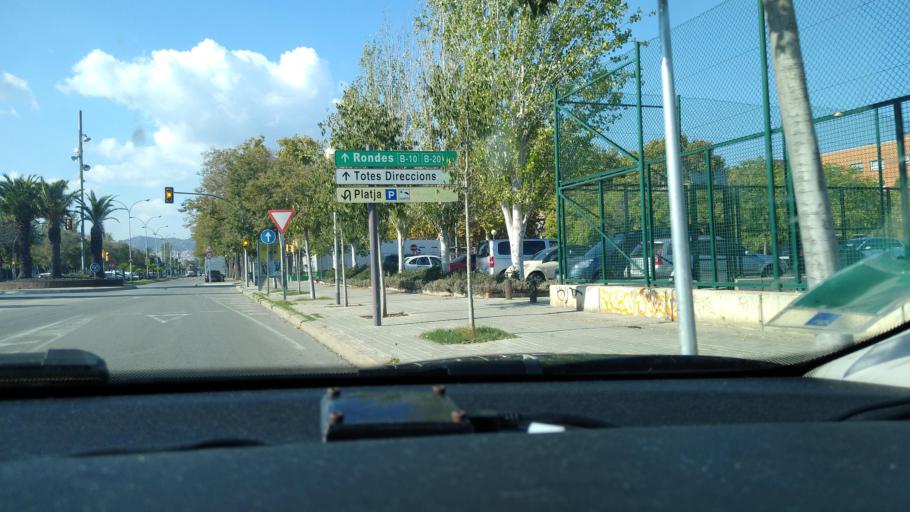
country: ES
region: Catalonia
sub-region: Provincia de Barcelona
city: Sant Adria de Besos
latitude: 41.4236
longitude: 2.2275
